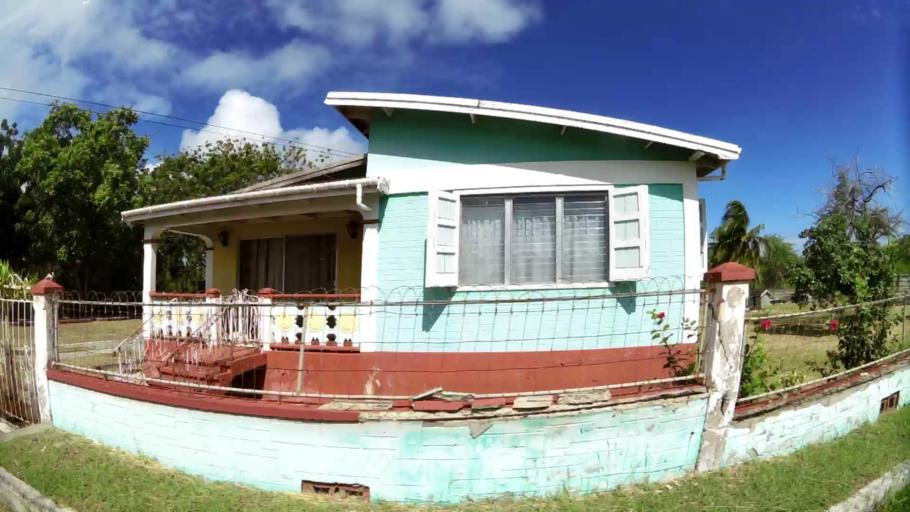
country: AG
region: Saint Paul
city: Falmouth
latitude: 17.0344
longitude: -61.7499
